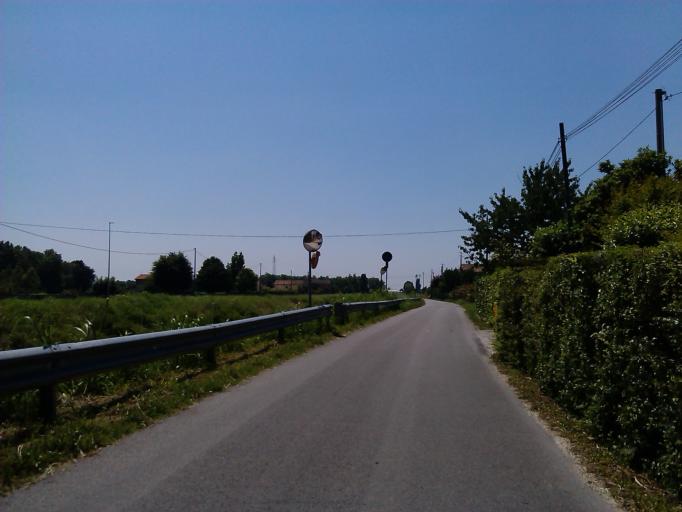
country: IT
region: Veneto
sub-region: Provincia di Treviso
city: Sant'Andrea
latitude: 45.6445
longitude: 11.9223
